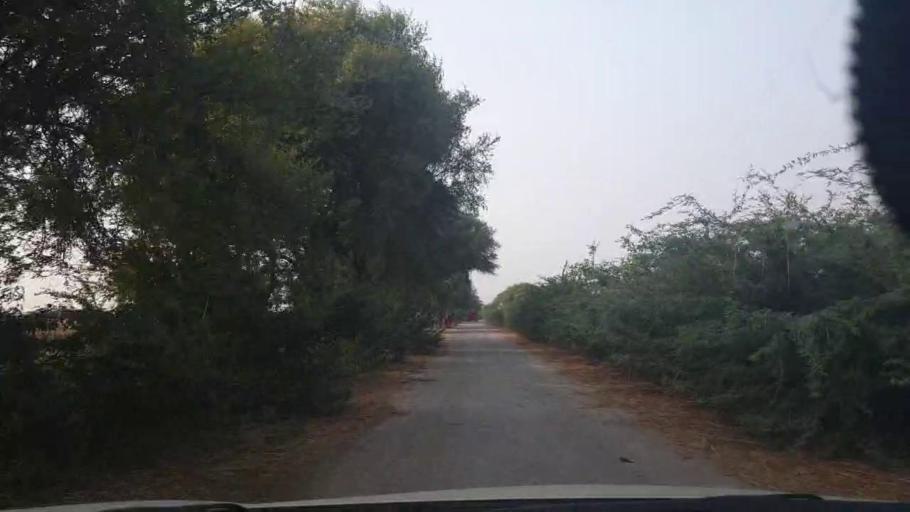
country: PK
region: Sindh
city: Bulri
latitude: 24.8070
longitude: 68.4100
